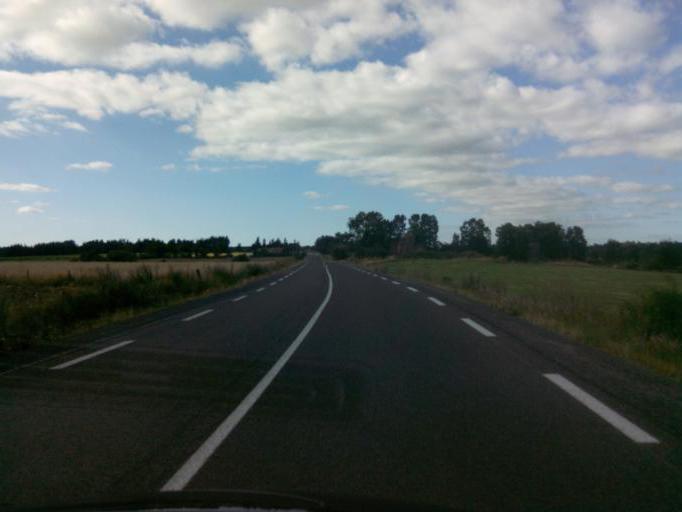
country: FR
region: Auvergne
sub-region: Departement de la Haute-Loire
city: Saint-Paulien
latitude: 45.1938
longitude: 3.8223
